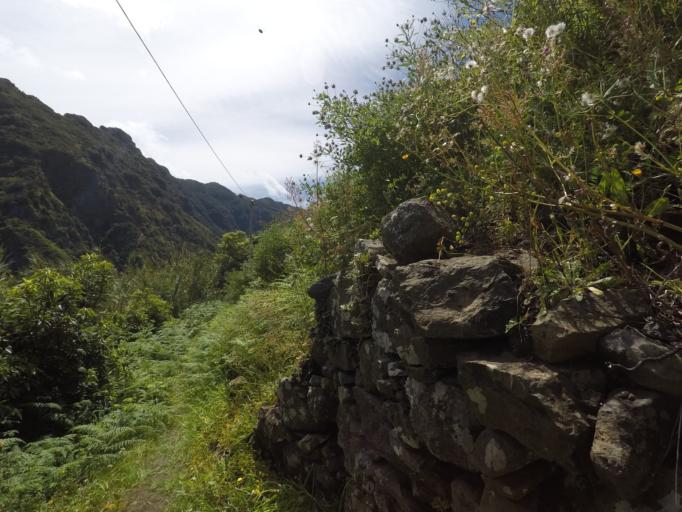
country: PT
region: Madeira
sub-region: Sao Vicente
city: Sao Vicente
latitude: 32.8251
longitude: -16.9727
